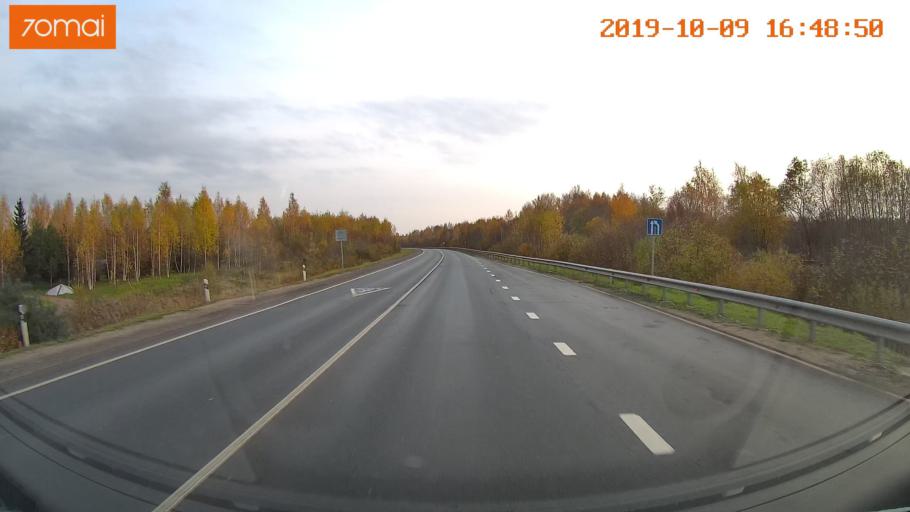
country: RU
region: Kostroma
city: Volgorechensk
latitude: 57.4234
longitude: 41.1908
